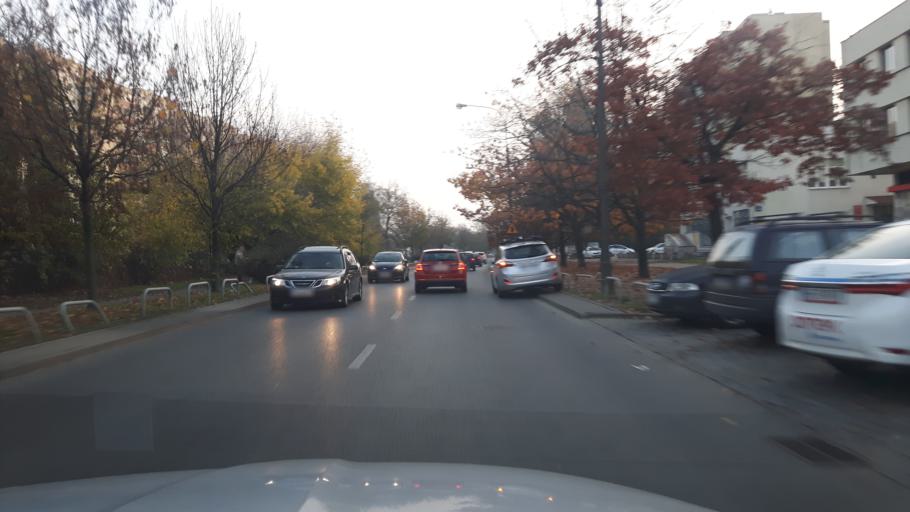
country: PL
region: Masovian Voivodeship
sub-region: Warszawa
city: Mokotow
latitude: 52.1784
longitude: 21.0139
